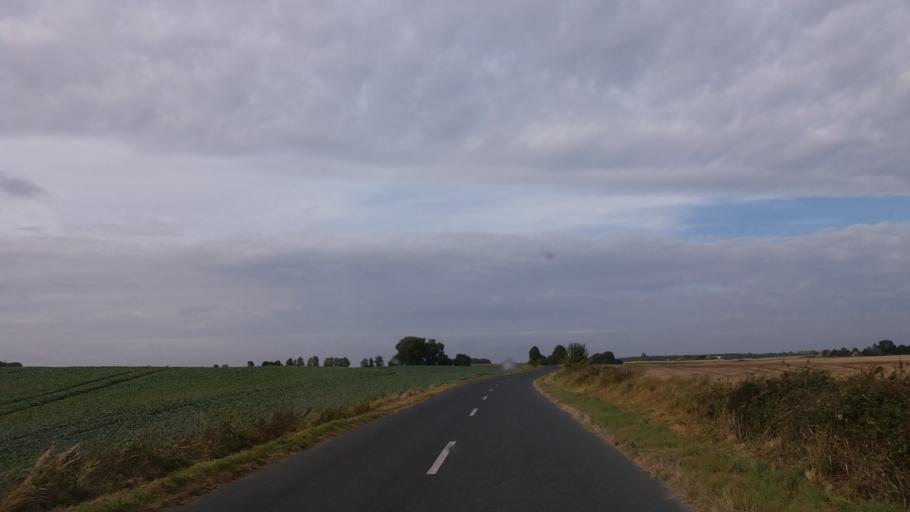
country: PL
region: West Pomeranian Voivodeship
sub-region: Powiat choszczenski
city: Krzecin
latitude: 53.0471
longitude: 15.4921
